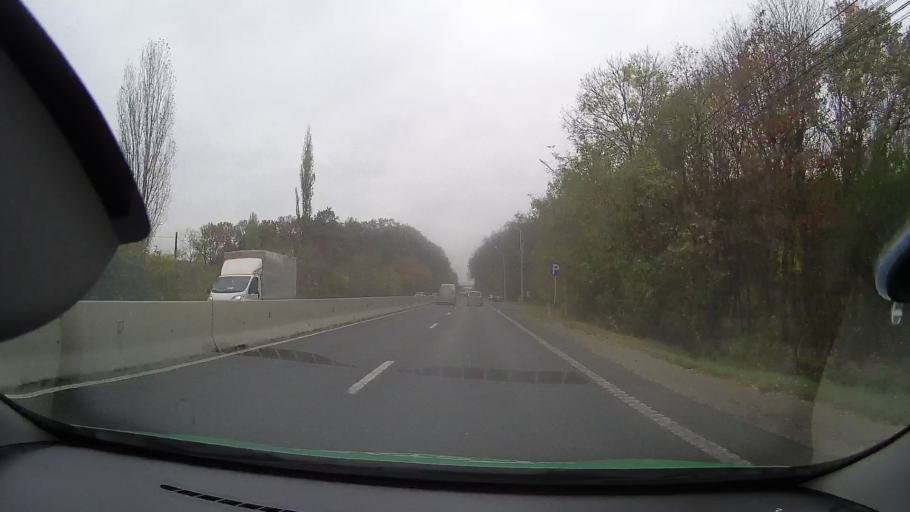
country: RO
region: Ilfov
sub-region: Comuna Corbeanca
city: Corbeanca
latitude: 44.5904
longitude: 26.0708
